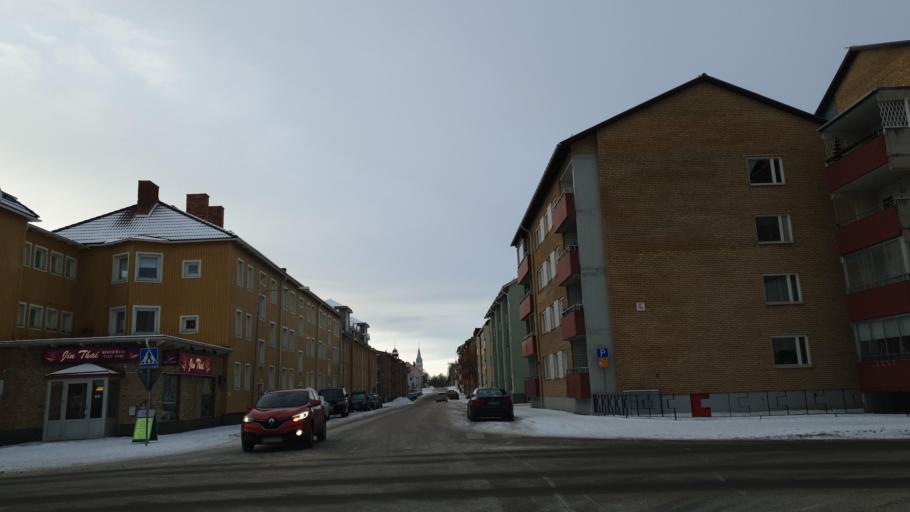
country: SE
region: Gaevleborg
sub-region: Soderhamns Kommun
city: Soderhamn
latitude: 61.3072
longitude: 17.0618
